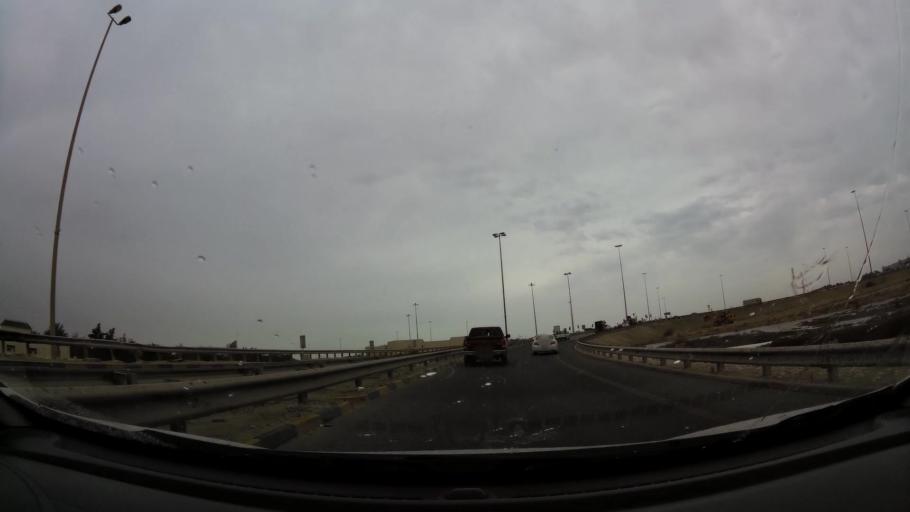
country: BH
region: Central Governorate
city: Madinat Hamad
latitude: 26.1694
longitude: 50.4657
